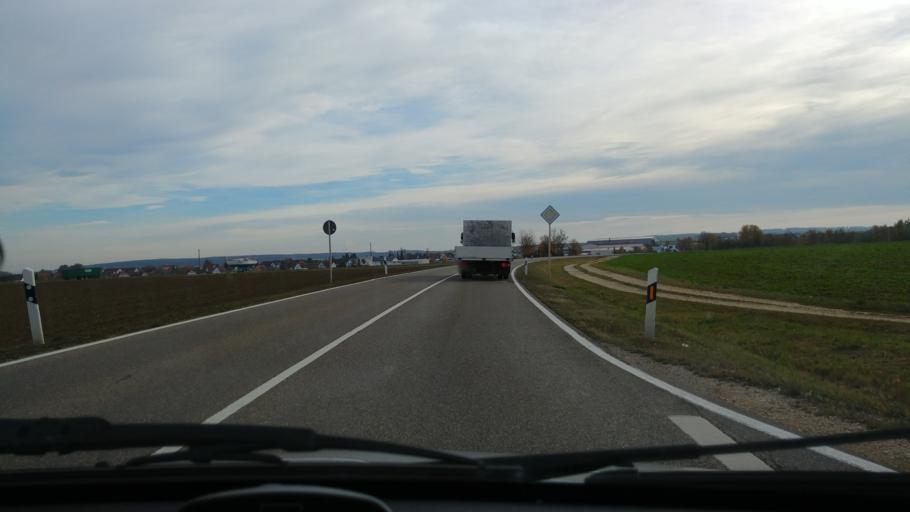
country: DE
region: Bavaria
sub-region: Swabia
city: Zoschingen
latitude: 48.6471
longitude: 10.2963
